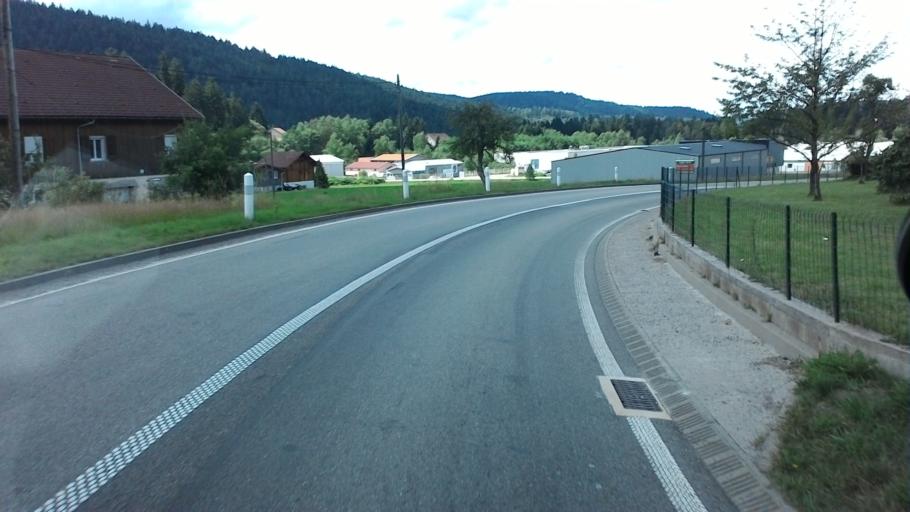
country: FR
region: Lorraine
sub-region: Departement des Vosges
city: Gerardmer
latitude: 48.0726
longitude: 6.8185
